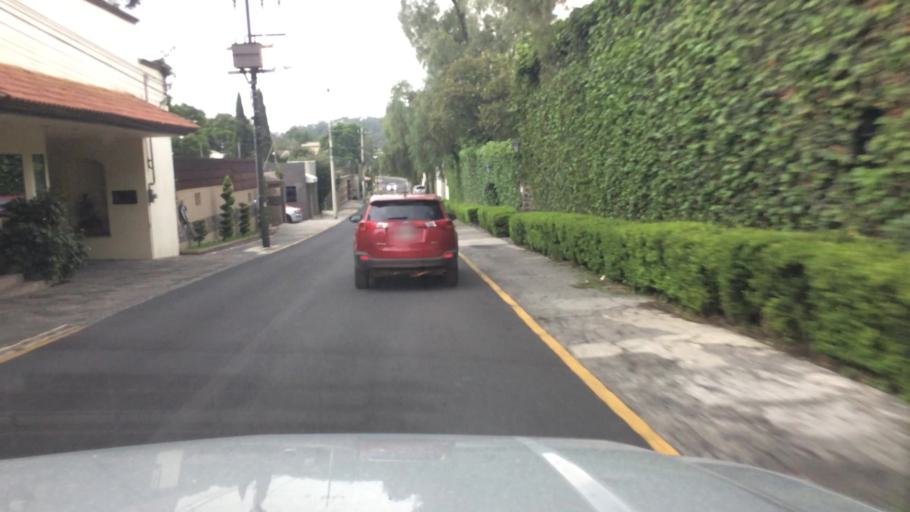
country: MX
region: Mexico City
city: Magdalena Contreras
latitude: 19.3162
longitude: -99.2080
